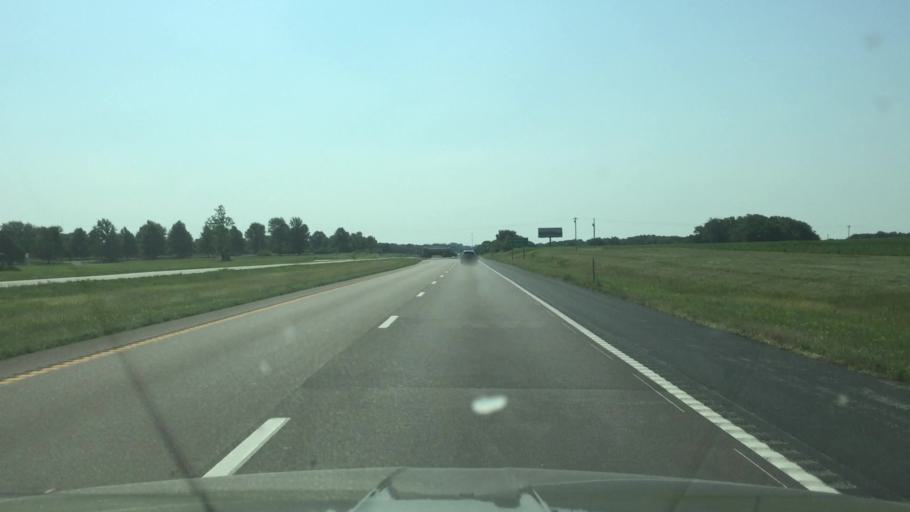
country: US
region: Missouri
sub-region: Pettis County
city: La Monte
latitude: 38.7488
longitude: -93.3441
